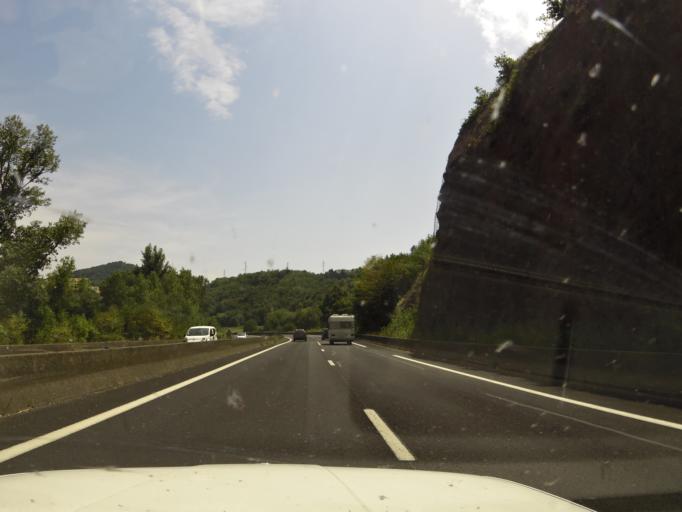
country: FR
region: Auvergne
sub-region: Departement du Puy-de-Dome
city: Vic-le-Comte
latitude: 45.6025
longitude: 3.2171
